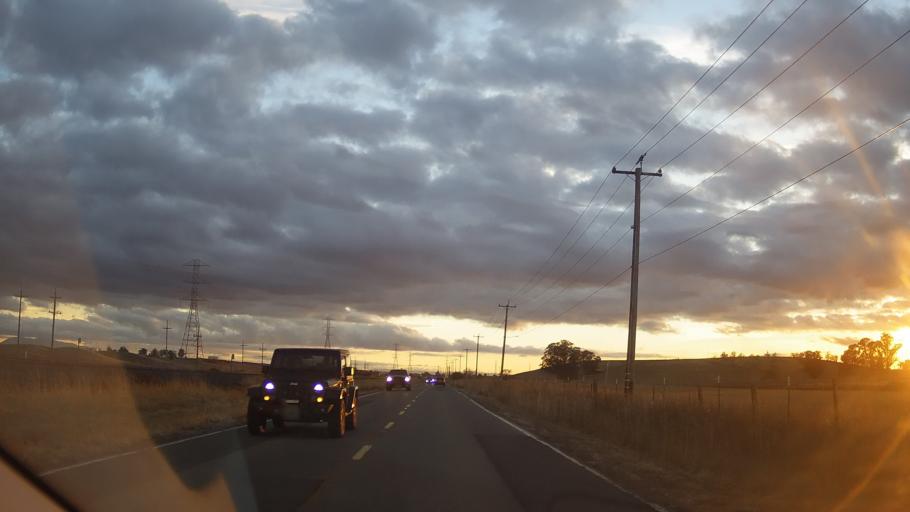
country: US
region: California
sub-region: Solano County
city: Vacaville
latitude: 38.3073
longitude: -121.9461
